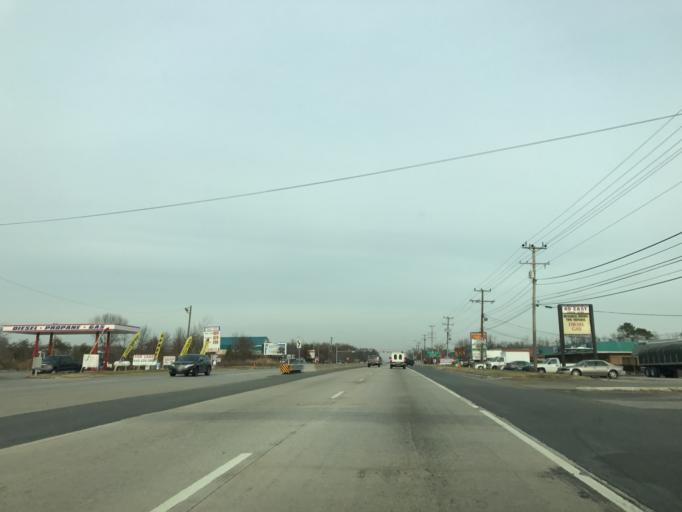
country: US
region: Maryland
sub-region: Baltimore County
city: White Marsh
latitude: 39.3957
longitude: -76.4071
